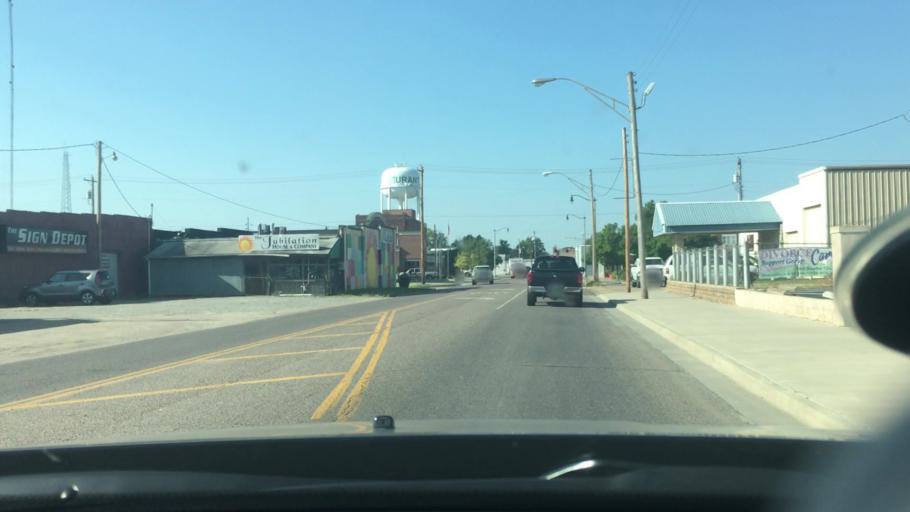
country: US
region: Oklahoma
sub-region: Bryan County
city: Durant
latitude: 33.9927
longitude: -96.3758
